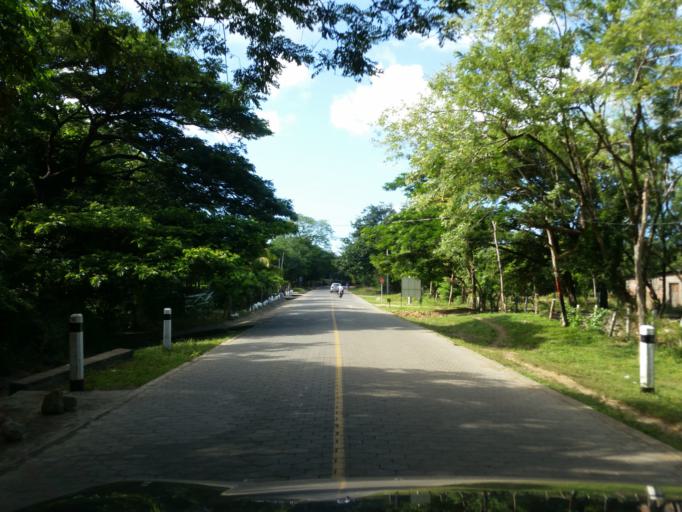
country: NI
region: Rivas
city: San Juan del Sur
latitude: 11.2478
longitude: -85.8490
